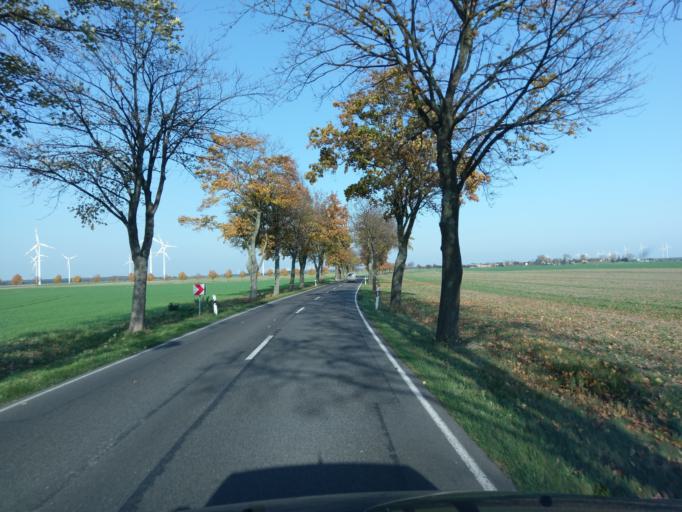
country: DE
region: Brandenburg
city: Muhlberg
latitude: 51.4551
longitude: 13.2404
